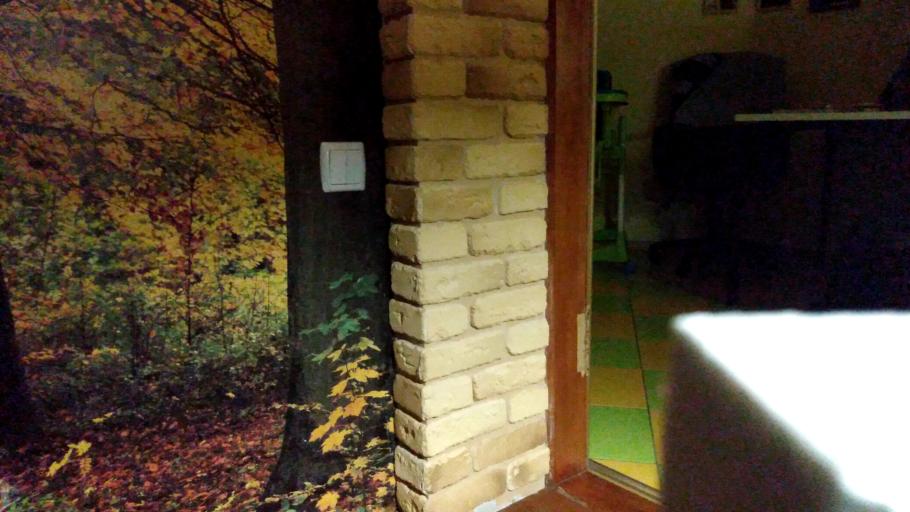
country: RU
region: Vologda
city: Lipin Bor
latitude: 60.9292
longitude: 37.9865
